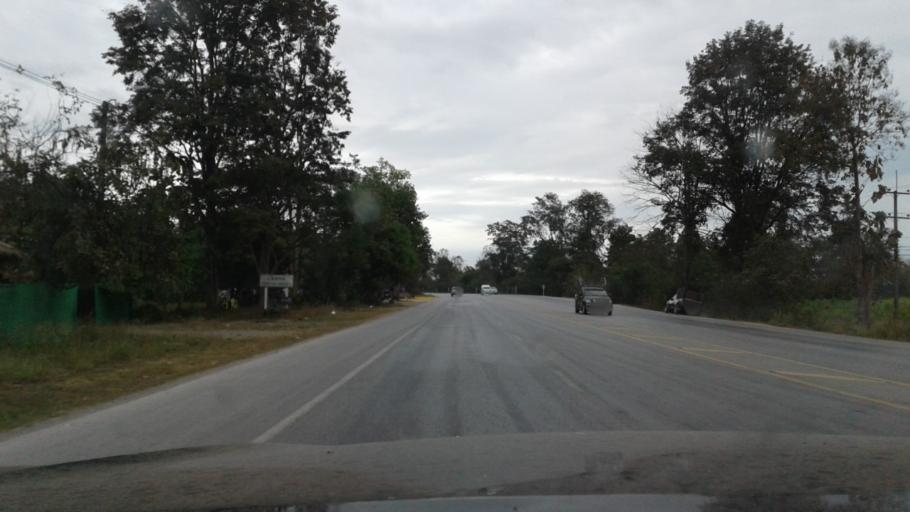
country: TH
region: Changwat Udon Thani
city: Nong Wua So
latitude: 17.2533
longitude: 102.5762
